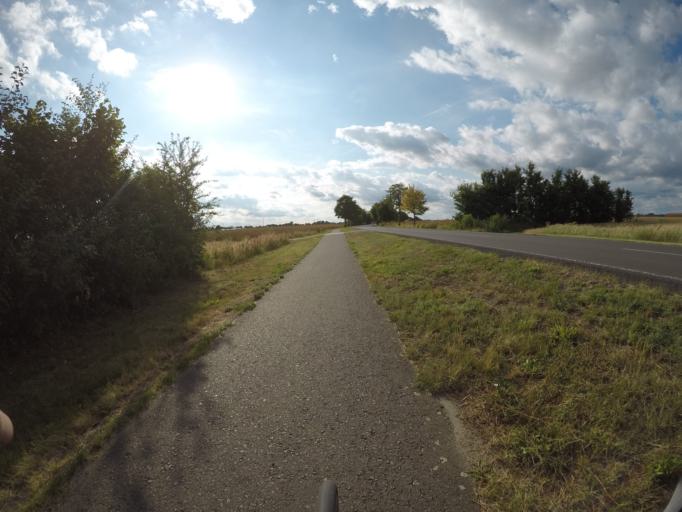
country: DE
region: Berlin
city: Falkenberg
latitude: 52.5899
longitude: 13.5530
